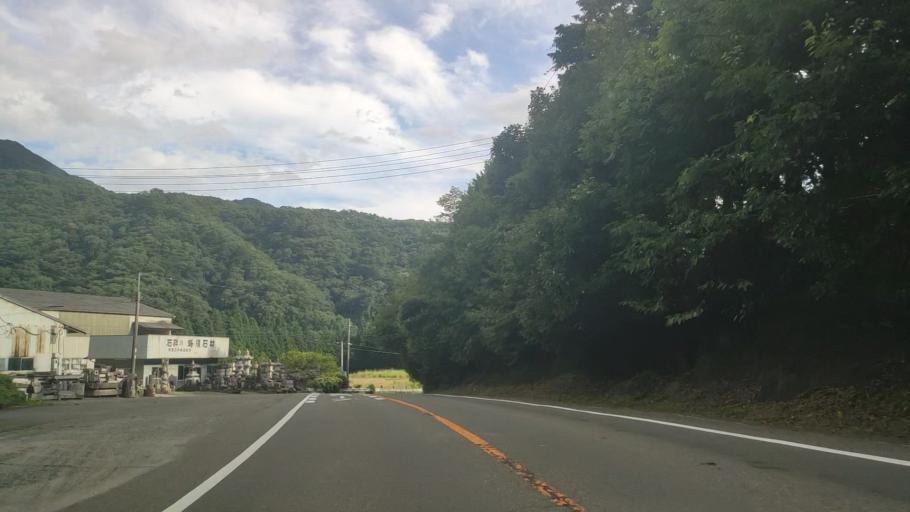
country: JP
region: Gunma
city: Kiryu
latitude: 36.5955
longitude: 139.4036
